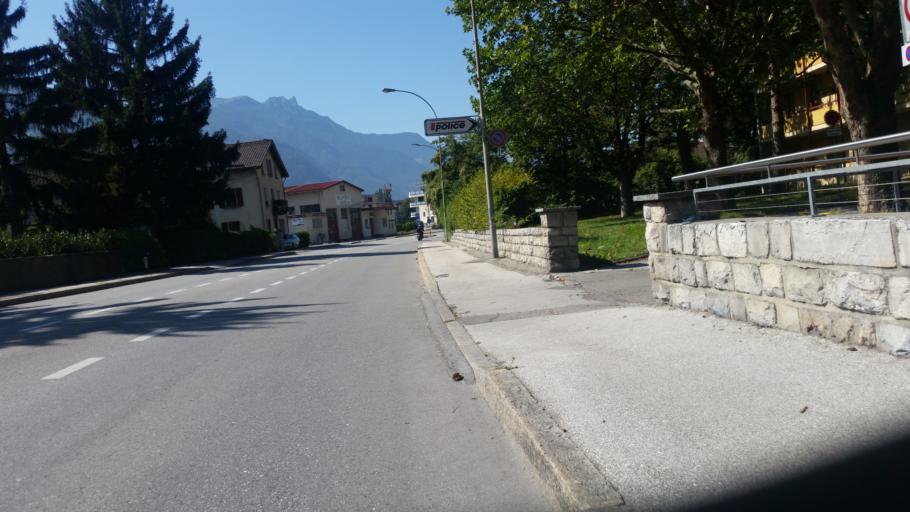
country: CH
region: Valais
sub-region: Conthey District
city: Ardon
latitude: 46.2094
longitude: 7.2568
